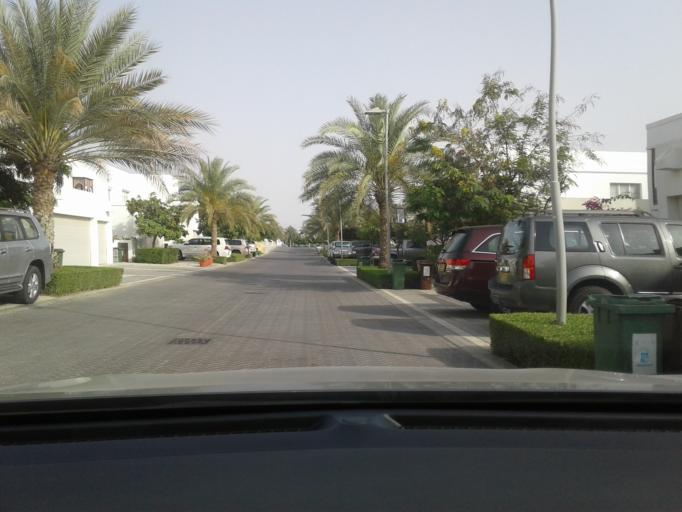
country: OM
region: Muhafazat Masqat
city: As Sib al Jadidah
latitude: 23.6243
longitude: 58.2727
